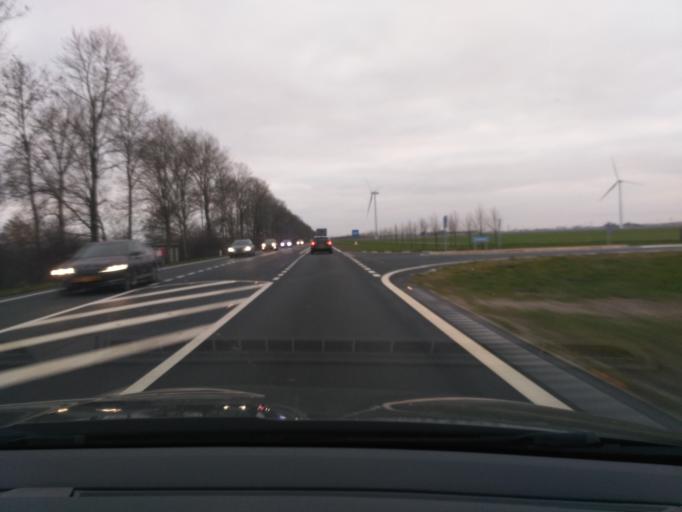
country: NL
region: Flevoland
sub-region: Gemeente Dronten
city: Biddinghuizen
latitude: 52.4435
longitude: 5.6599
